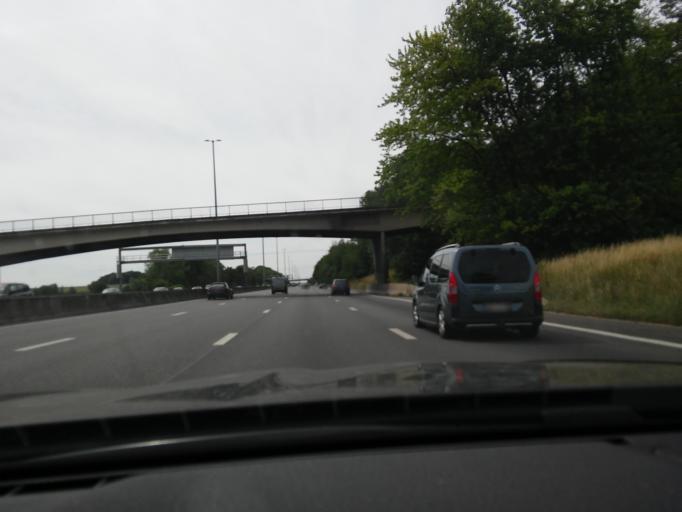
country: BE
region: Flanders
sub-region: Provincie Vlaams-Brabant
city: Bertem
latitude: 50.8642
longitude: 4.5916
